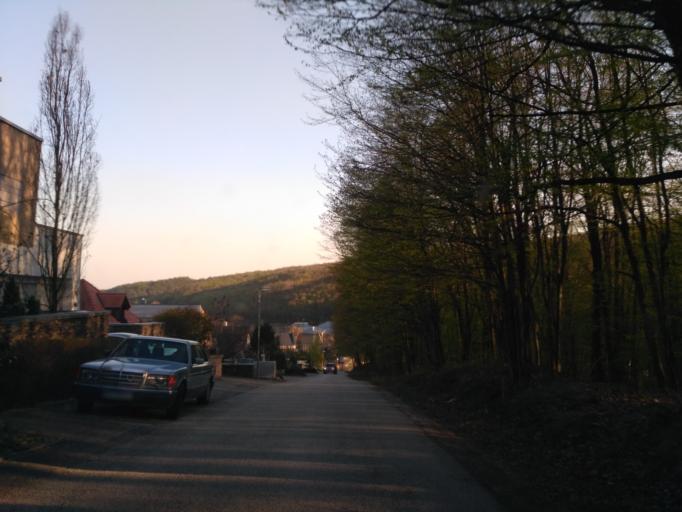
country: SK
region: Kosicky
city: Kosice
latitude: 48.7166
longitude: 21.1947
